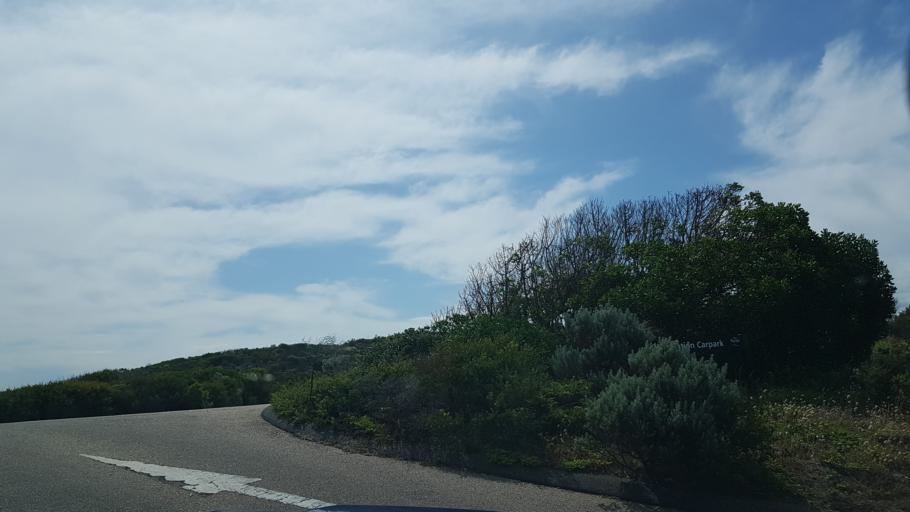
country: AU
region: Victoria
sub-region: Mornington Peninsula
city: Sorrento
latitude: -38.3341
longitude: 144.7065
